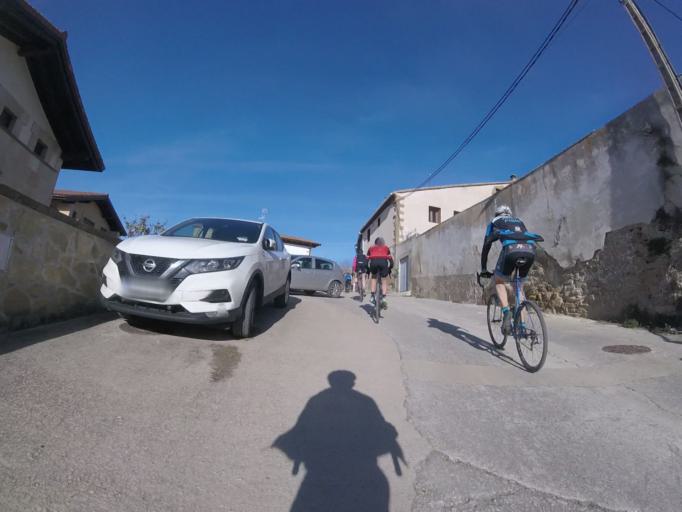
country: ES
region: Navarre
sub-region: Provincia de Navarra
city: Yerri
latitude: 42.6935
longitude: -1.9587
